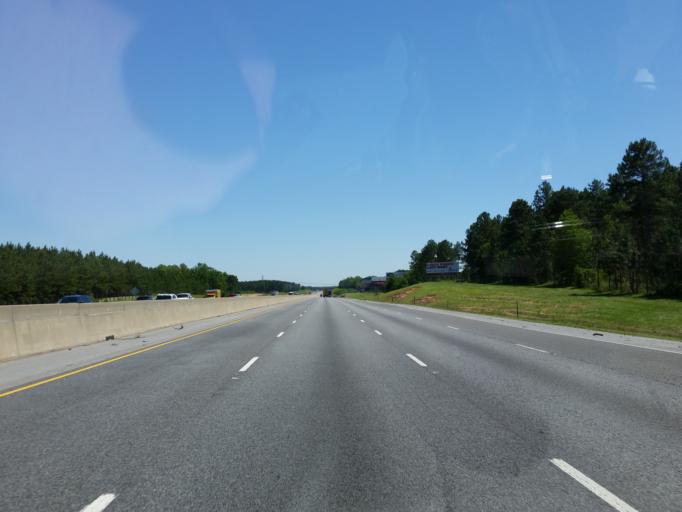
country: US
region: Georgia
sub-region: Tift County
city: Tifton
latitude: 31.5468
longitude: -83.5326
